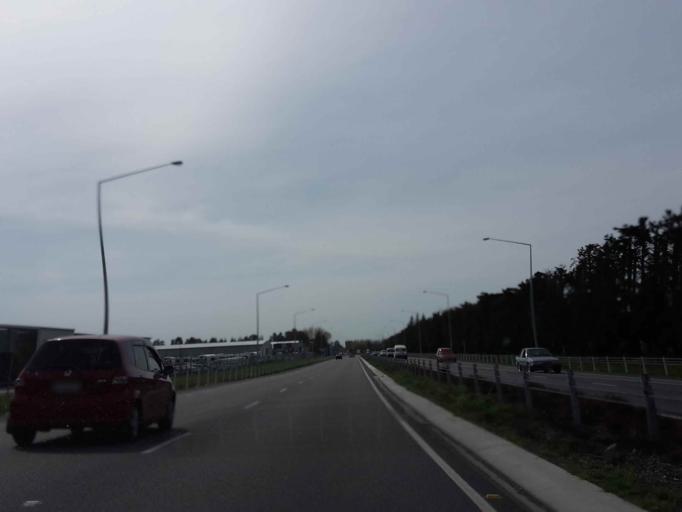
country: NZ
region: Canterbury
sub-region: Christchurch City
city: Christchurch
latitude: -43.4736
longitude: 172.5618
